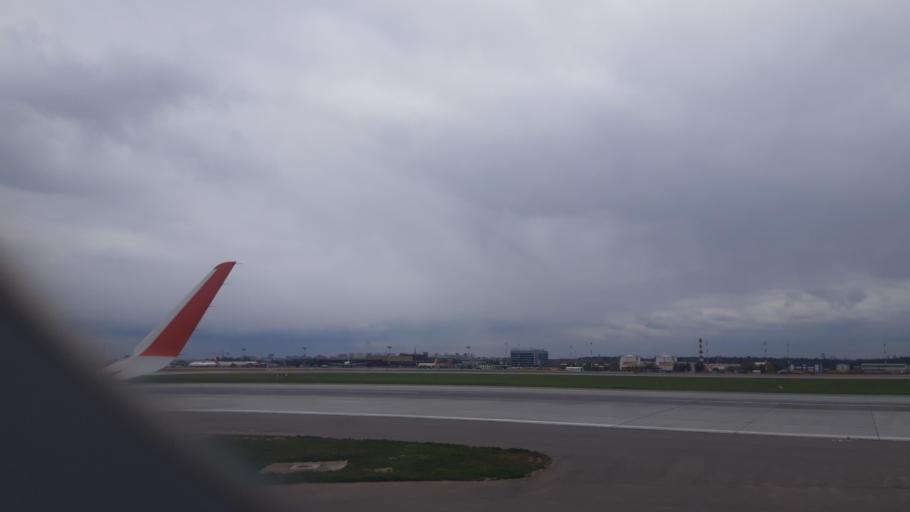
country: RU
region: Moskovskaya
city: Lobnya
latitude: 55.9758
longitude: 37.4224
